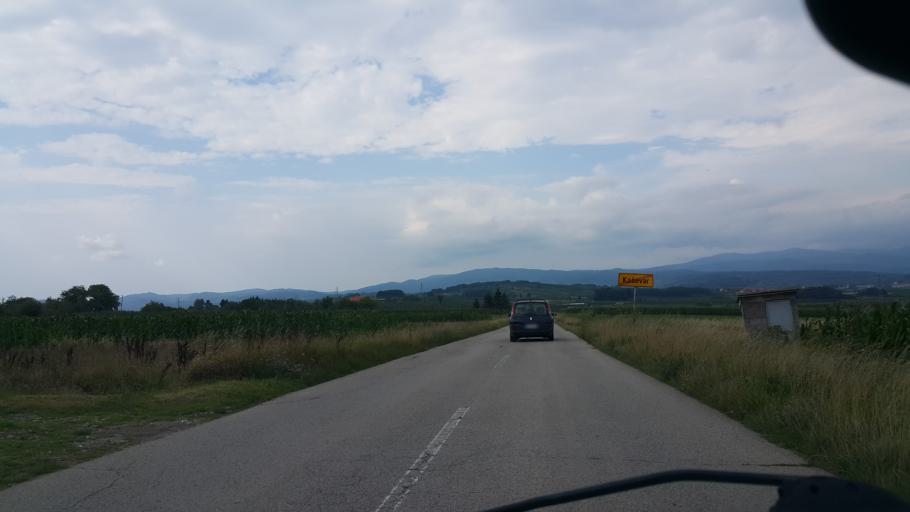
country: RS
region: Central Serbia
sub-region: Toplicki Okrug
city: Blace
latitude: 43.2669
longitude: 21.2734
